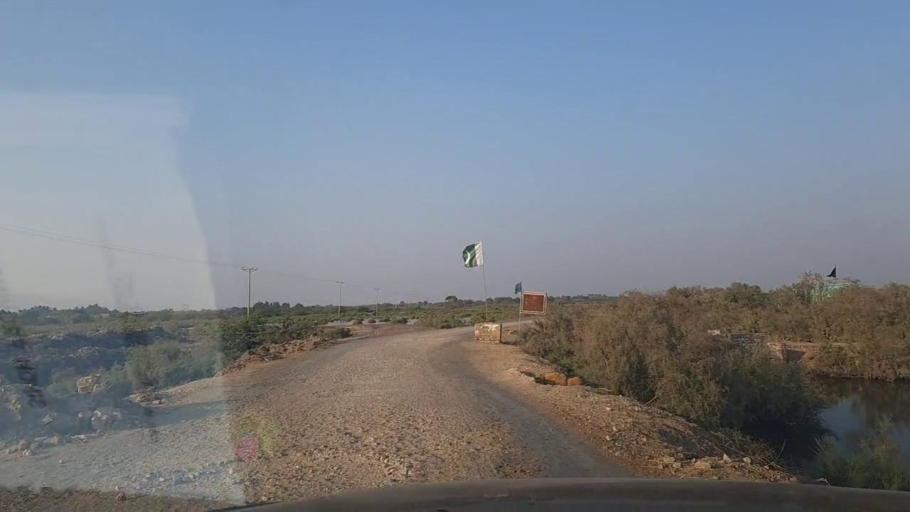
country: PK
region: Sindh
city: Keti Bandar
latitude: 24.2756
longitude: 67.5868
